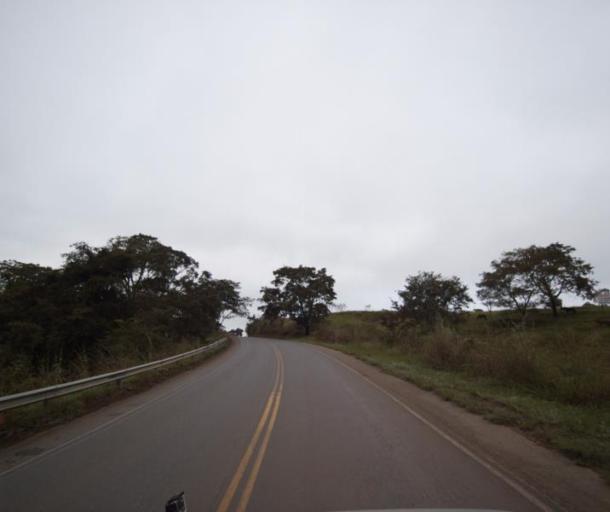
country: BR
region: Goias
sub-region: Pirenopolis
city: Pirenopolis
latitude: -15.9041
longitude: -48.8006
